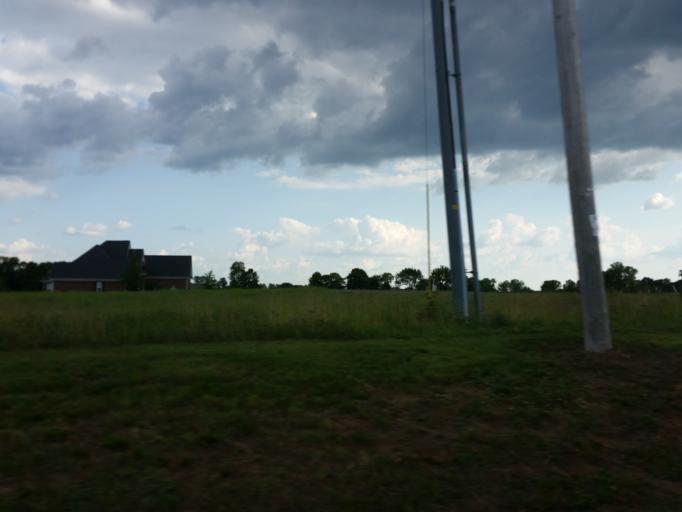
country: US
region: Tennessee
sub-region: Maury County
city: Mount Pleasant
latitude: 35.6139
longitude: -87.1519
